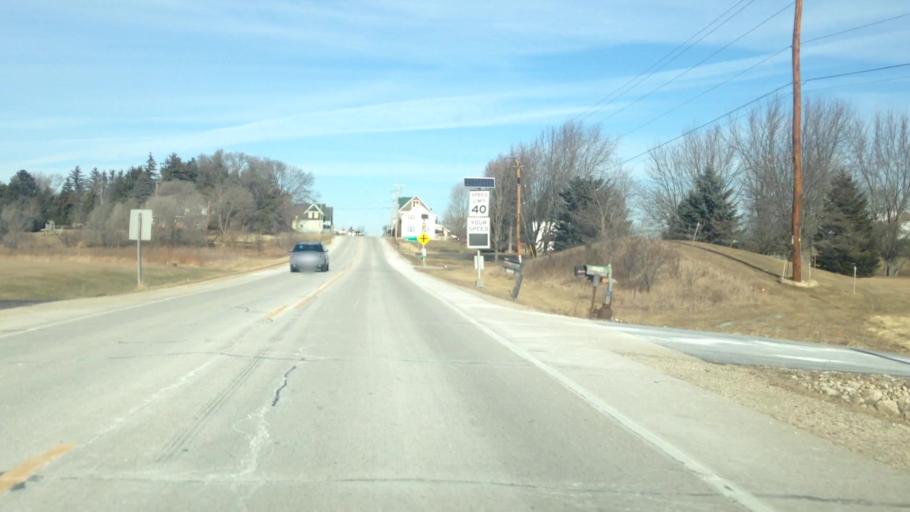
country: US
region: Wisconsin
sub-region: Washington County
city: Richfield
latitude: 43.2636
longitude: -88.2616
